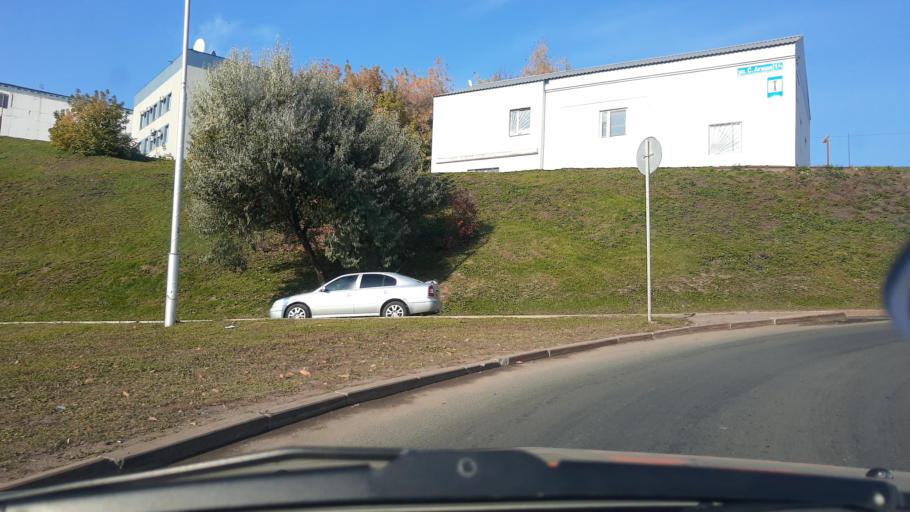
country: RU
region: Bashkortostan
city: Ufa
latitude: 54.7299
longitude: 55.9961
